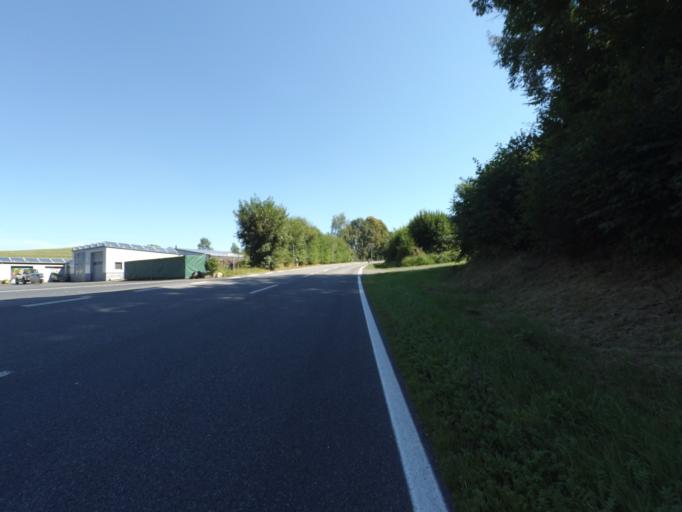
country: DE
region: Rheinland-Pfalz
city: Alflen
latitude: 50.1785
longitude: 7.0435
